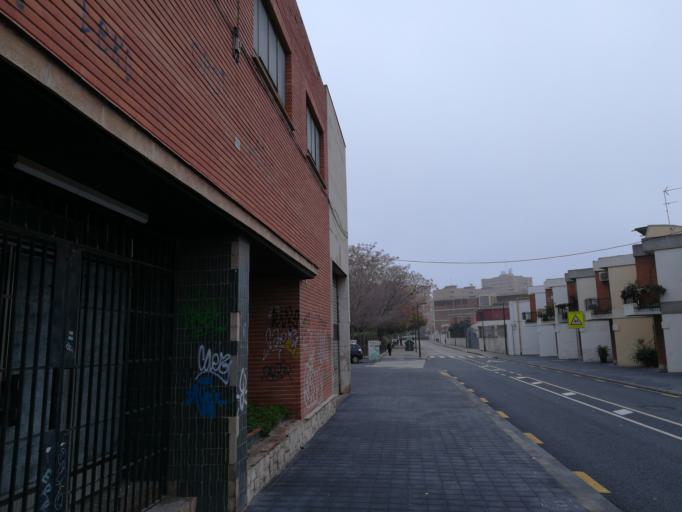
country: ES
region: Valencia
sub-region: Provincia de Valencia
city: Mislata
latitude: 39.4881
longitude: -0.4004
